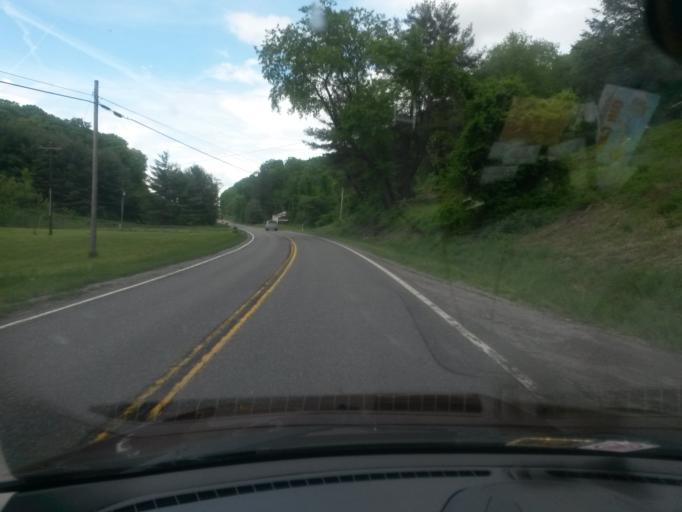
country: US
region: Virginia
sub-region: Montgomery County
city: Christiansburg
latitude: 37.1059
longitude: -80.4282
